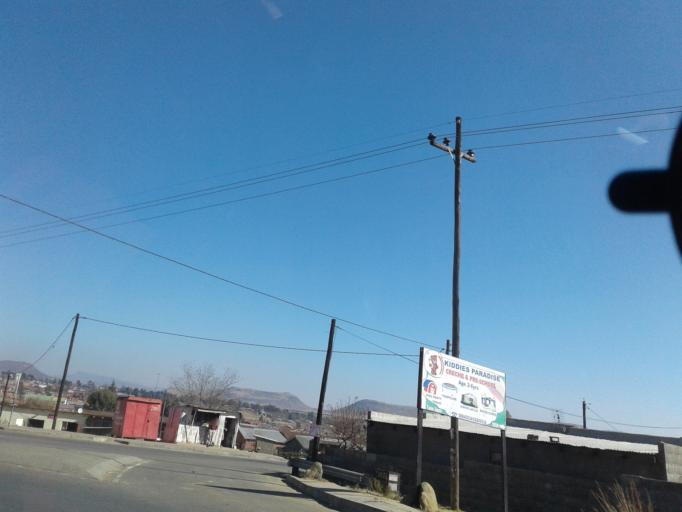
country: LS
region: Maseru
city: Maseru
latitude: -29.2896
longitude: 27.5217
